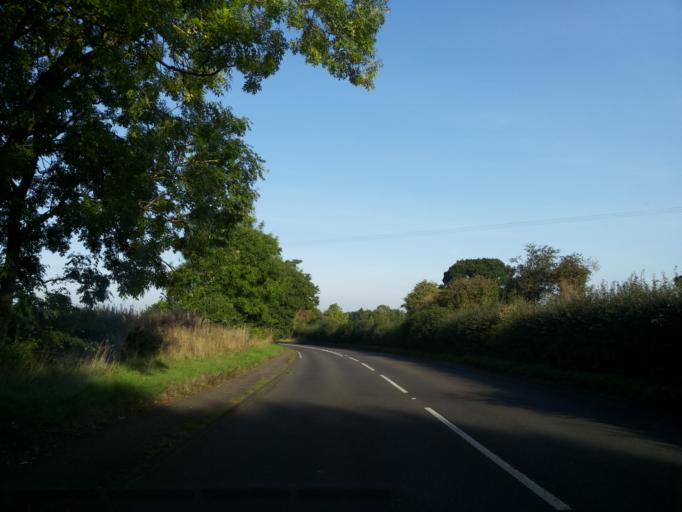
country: GB
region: England
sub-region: Warwickshire
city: Wroxall
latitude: 52.3580
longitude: -1.7019
